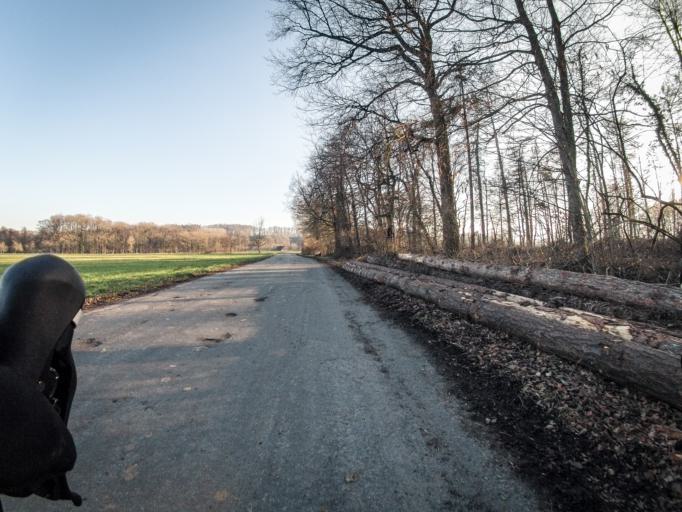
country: DE
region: North Rhine-Westphalia
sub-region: Regierungsbezirk Munster
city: Tecklenburg
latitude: 52.2528
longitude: 7.8332
